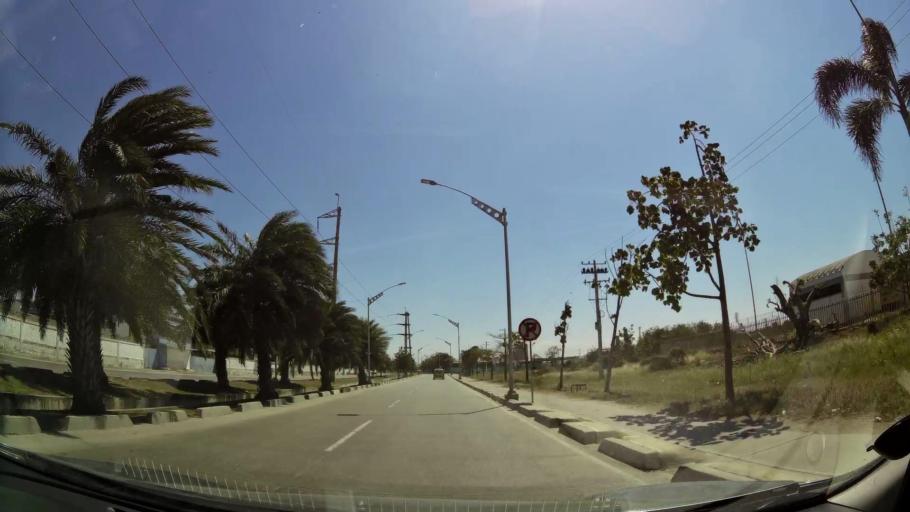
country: CO
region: Atlantico
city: Barranquilla
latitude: 10.9855
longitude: -74.7705
